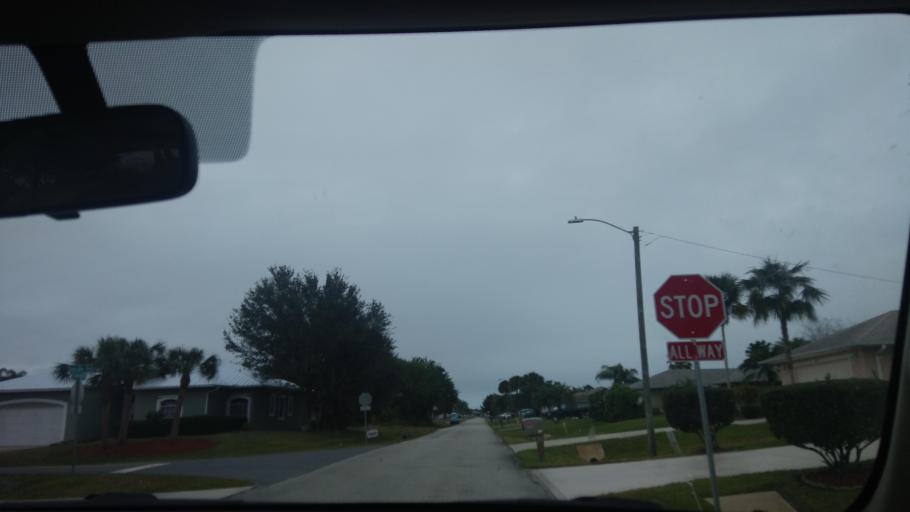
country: US
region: Florida
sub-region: Indian River County
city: Sebastian
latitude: 27.7807
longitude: -80.4790
